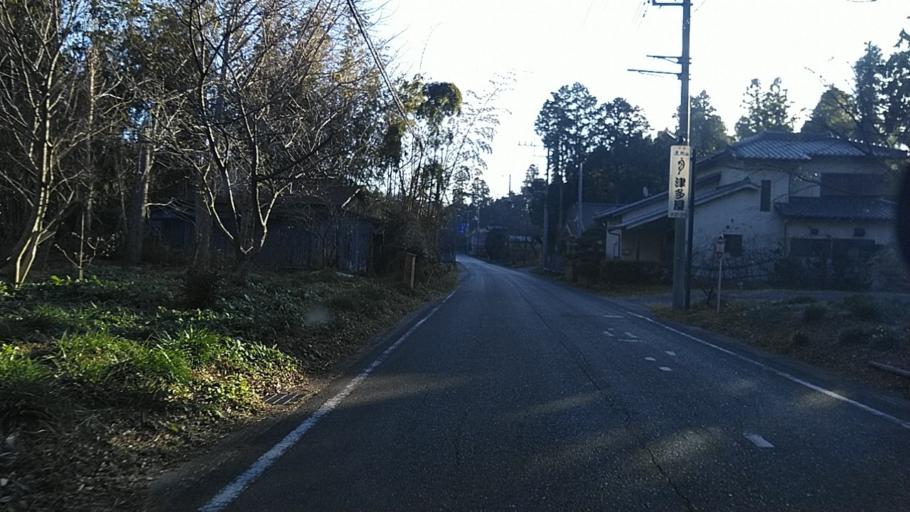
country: JP
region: Chiba
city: Kimitsu
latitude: 35.2542
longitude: 139.9657
